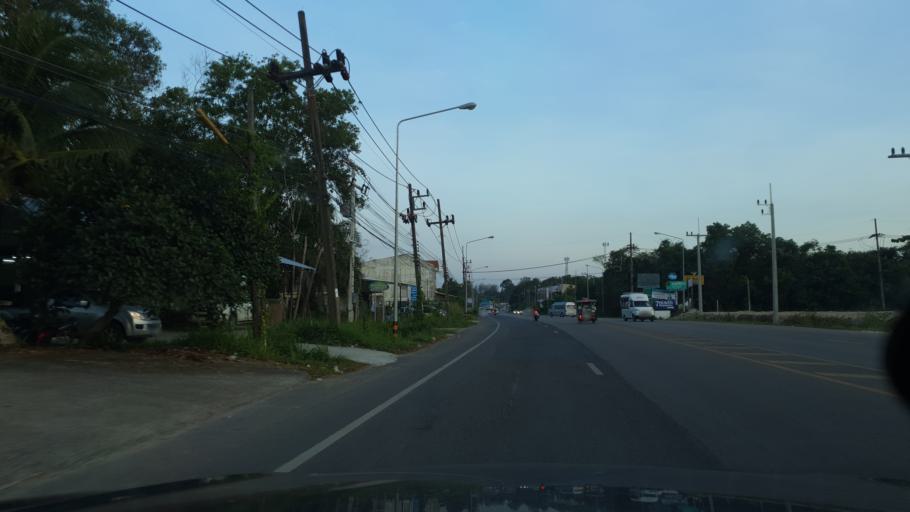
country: TH
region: Phangnga
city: Ban Ao Nang
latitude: 8.0351
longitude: 98.8577
